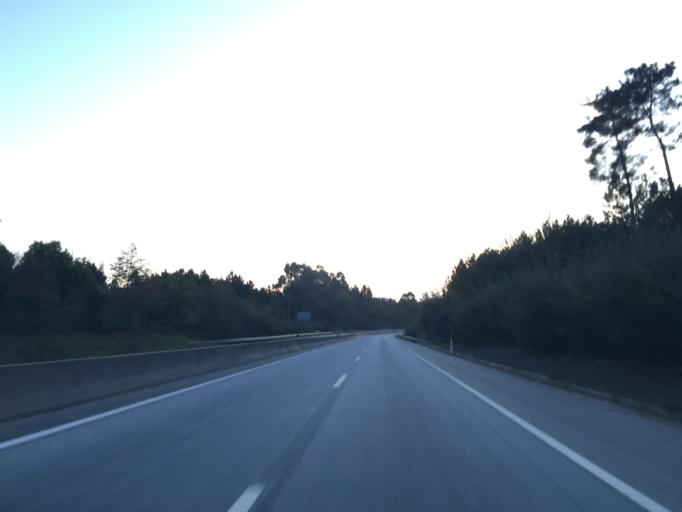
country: PT
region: Viseu
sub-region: Concelho de Carregal do Sal
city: Carregal do Sal
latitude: 40.4193
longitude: -8.0346
